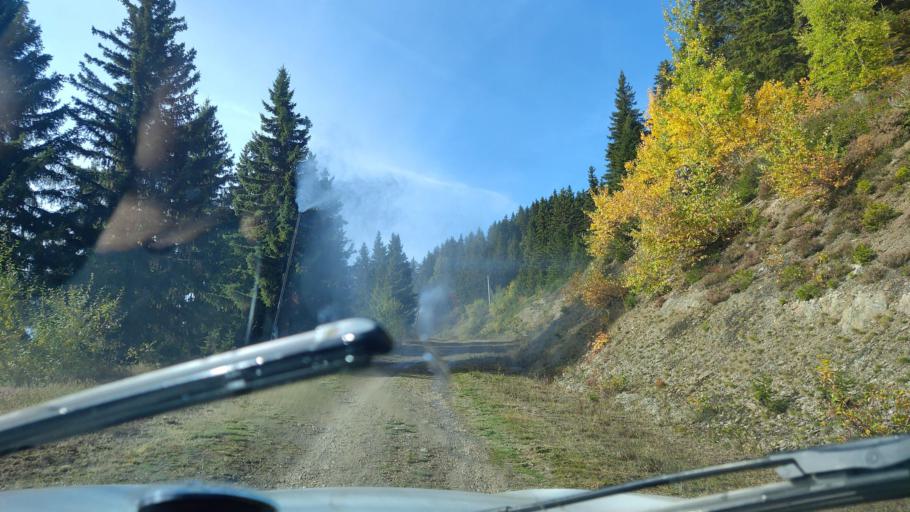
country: FR
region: Rhone-Alpes
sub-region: Departement de la Savoie
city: Ugine
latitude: 45.7380
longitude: 6.4918
